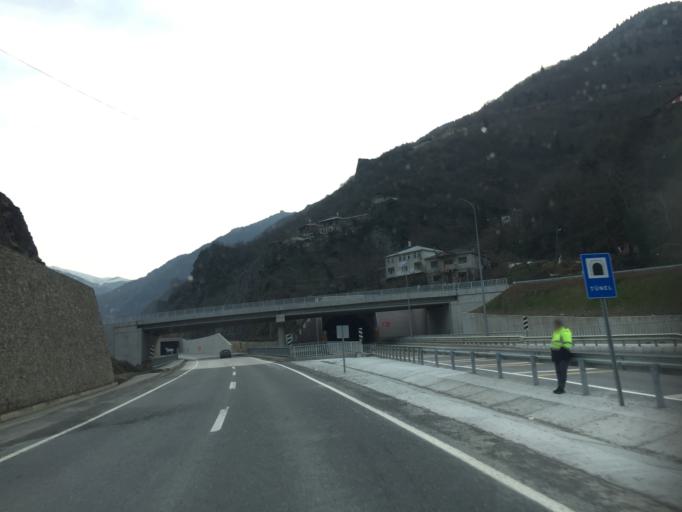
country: TR
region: Trabzon
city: Macka
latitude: 40.7798
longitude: 39.5700
